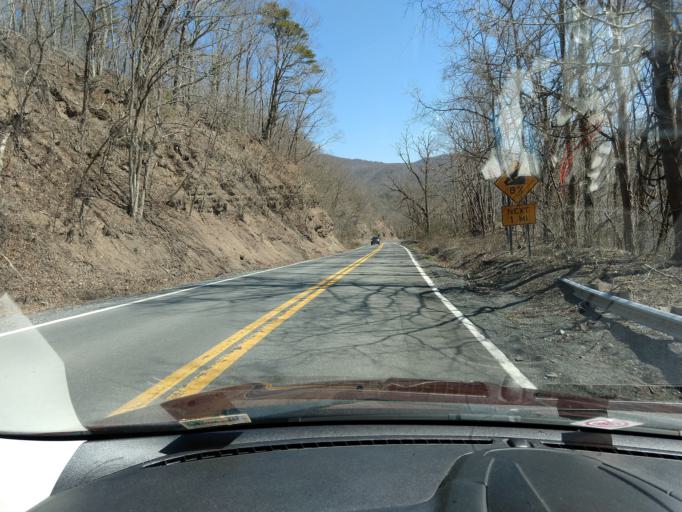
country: US
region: West Virginia
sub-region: Summers County
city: Hinton
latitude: 37.7365
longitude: -80.9063
